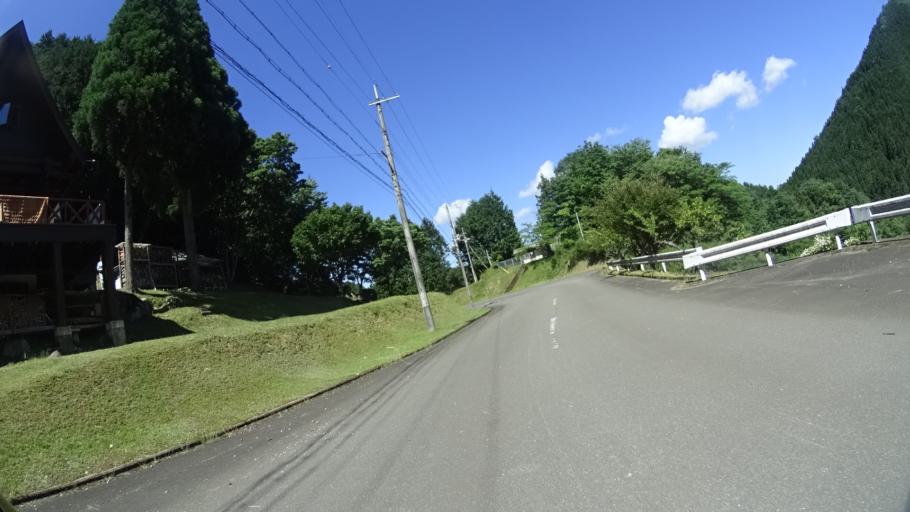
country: JP
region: Kyoto
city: Fukuchiyama
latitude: 35.3783
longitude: 135.0599
